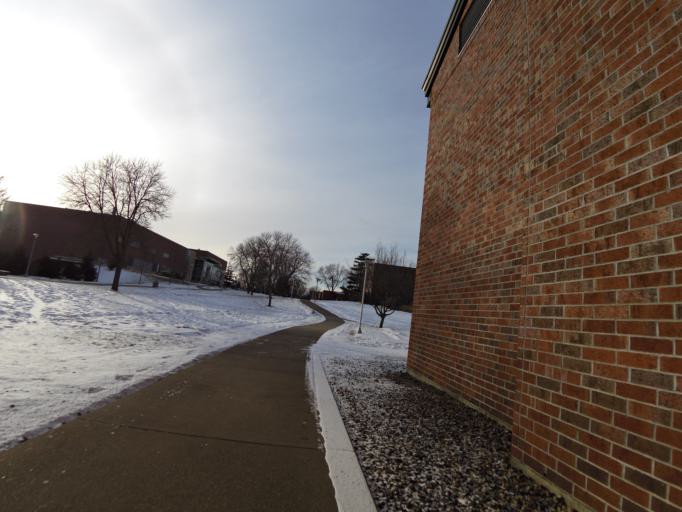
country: US
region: Wisconsin
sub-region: Pierce County
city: River Falls
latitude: 44.8529
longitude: -92.6196
